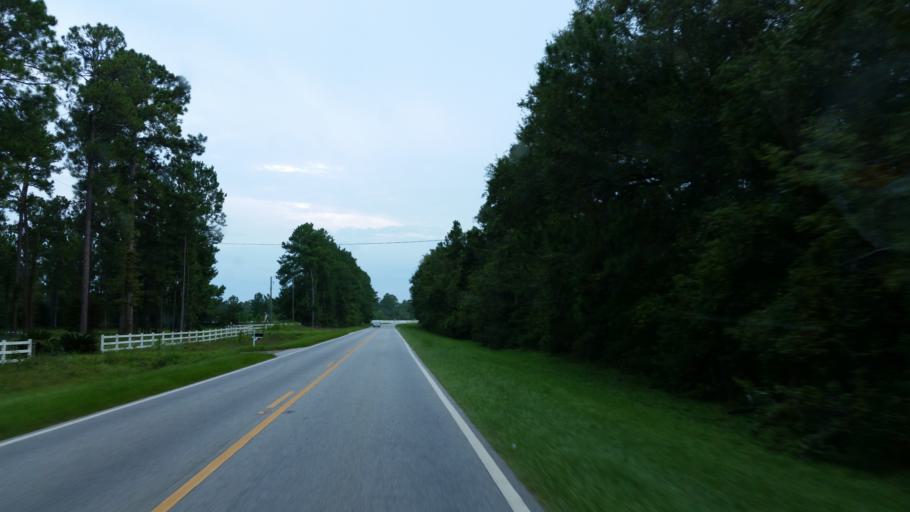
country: US
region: Georgia
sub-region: Lowndes County
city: Valdosta
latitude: 30.7616
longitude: -83.3042
